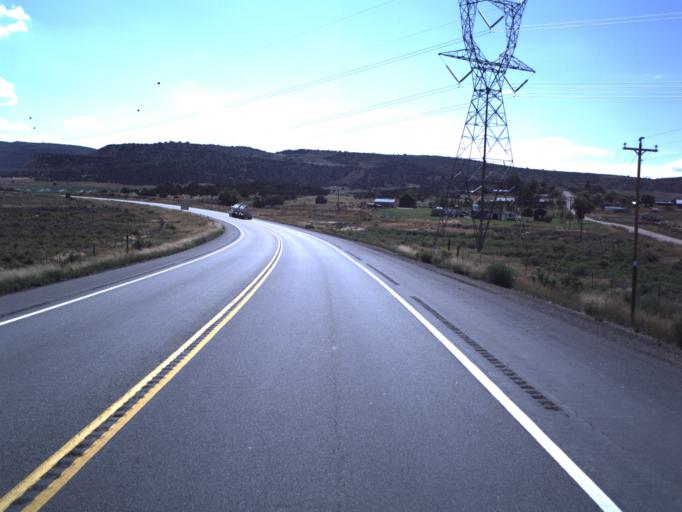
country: US
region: Utah
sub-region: Duchesne County
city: Duchesne
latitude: 40.2122
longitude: -110.8626
